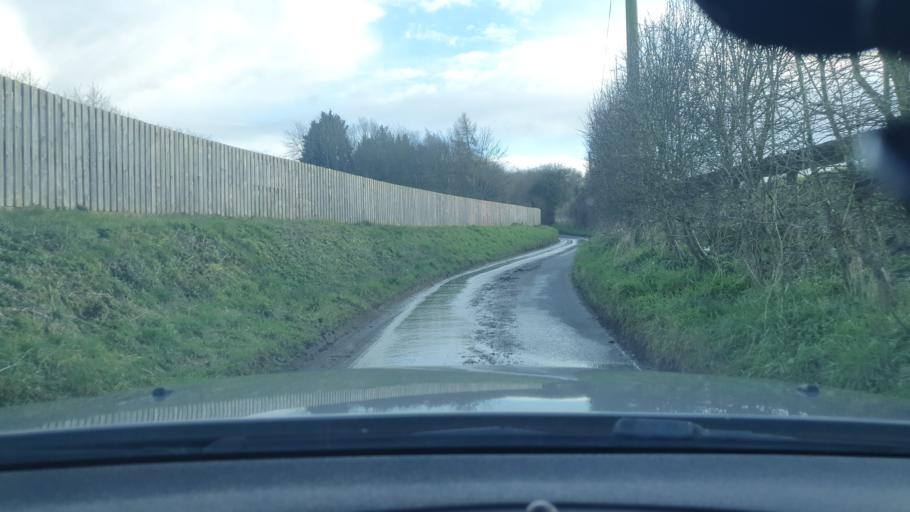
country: GB
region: England
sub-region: Wokingham
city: Wargrave
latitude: 51.5265
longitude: -0.8419
